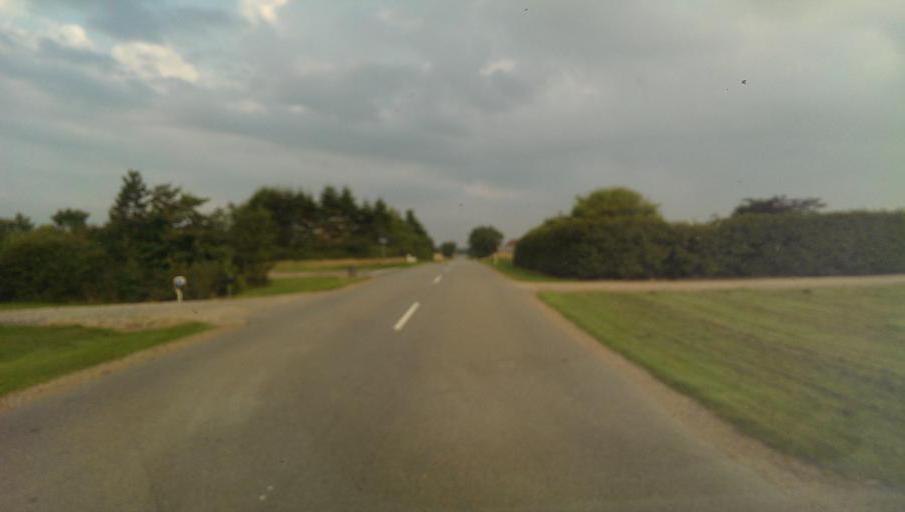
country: DK
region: South Denmark
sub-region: Varde Kommune
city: Varde
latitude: 55.5761
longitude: 8.5698
